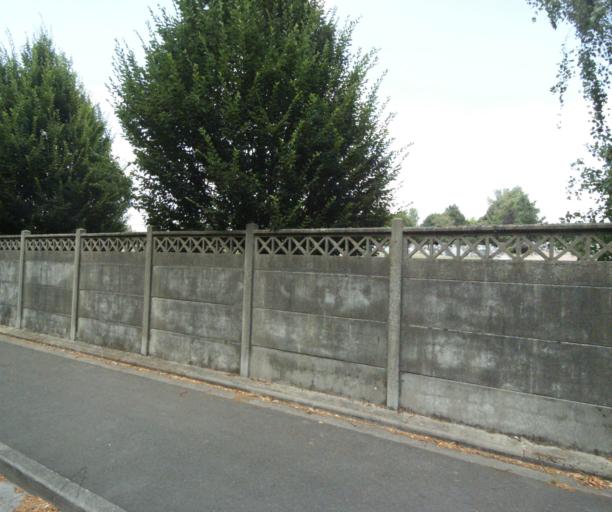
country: FR
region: Nord-Pas-de-Calais
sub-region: Departement du Nord
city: Saint-Andre-lez-Lille
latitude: 50.6659
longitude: 3.0524
